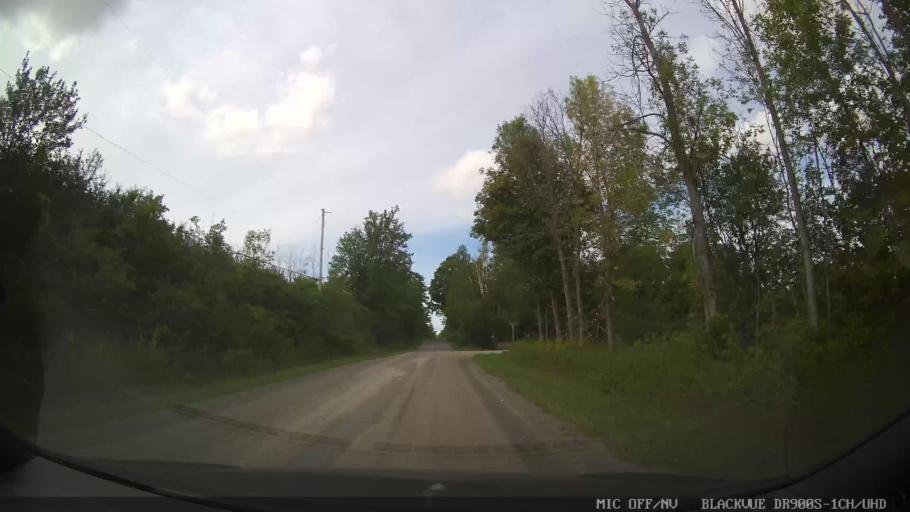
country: CA
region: Ontario
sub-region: Lanark County
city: Smiths Falls
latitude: 44.9270
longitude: -75.8763
